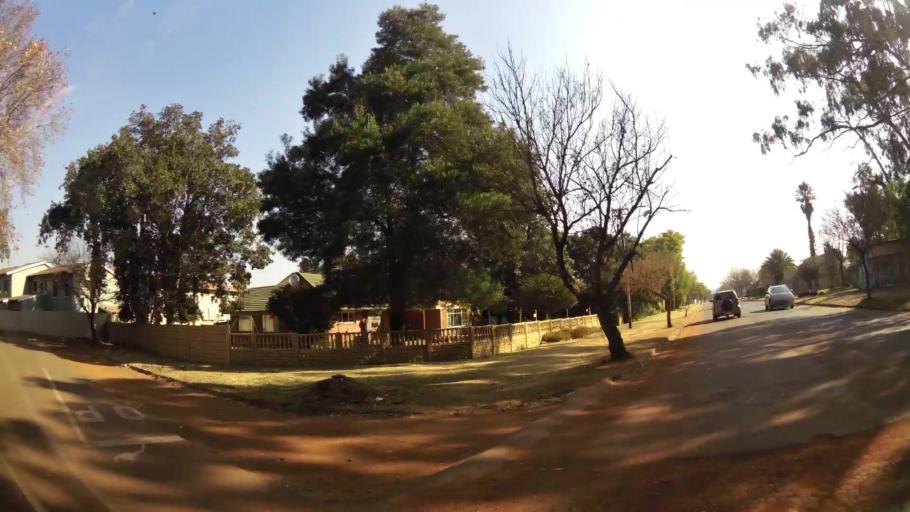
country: ZA
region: Gauteng
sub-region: West Rand District Municipality
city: Randfontein
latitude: -26.1657
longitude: 27.7028
